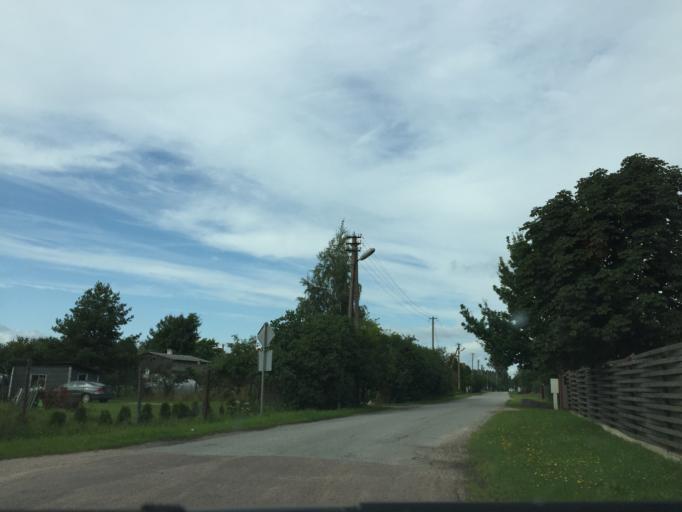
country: LV
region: Ogre
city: Ogre
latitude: 56.7691
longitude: 24.6463
